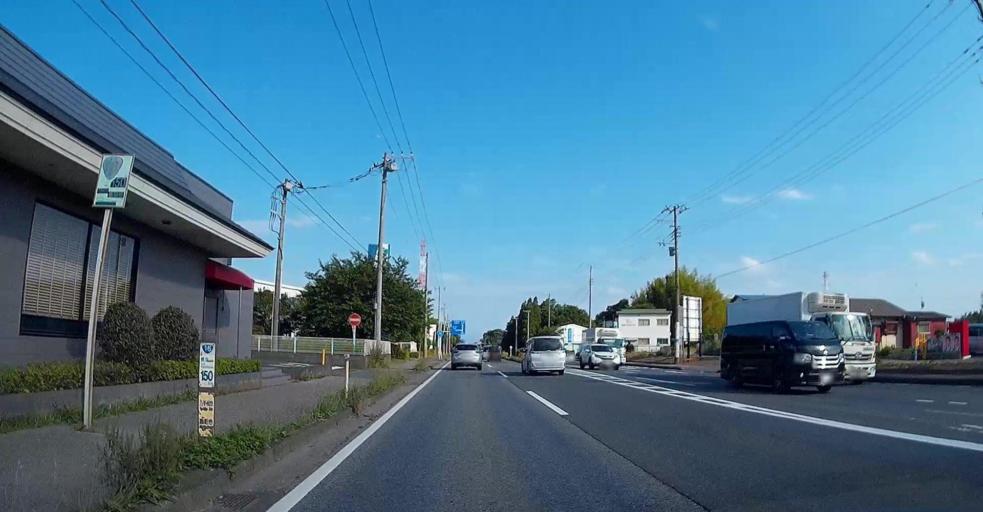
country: JP
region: Chiba
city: Shiroi
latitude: 35.7683
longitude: 140.0986
